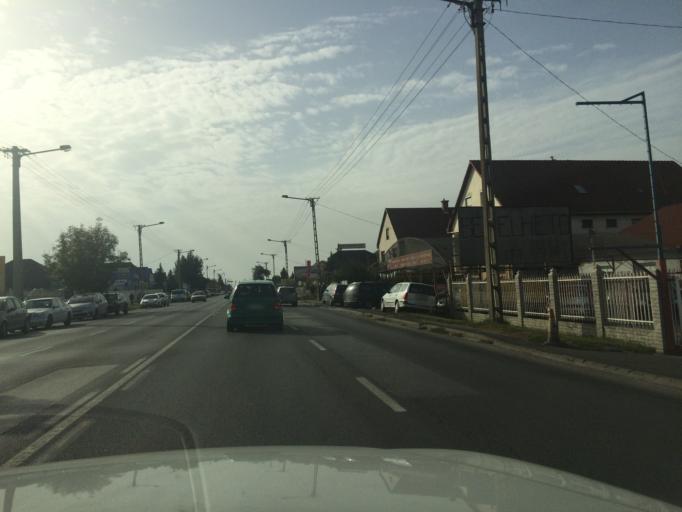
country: HU
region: Szabolcs-Szatmar-Bereg
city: Nyiregyhaza
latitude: 47.9288
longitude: 21.7187
